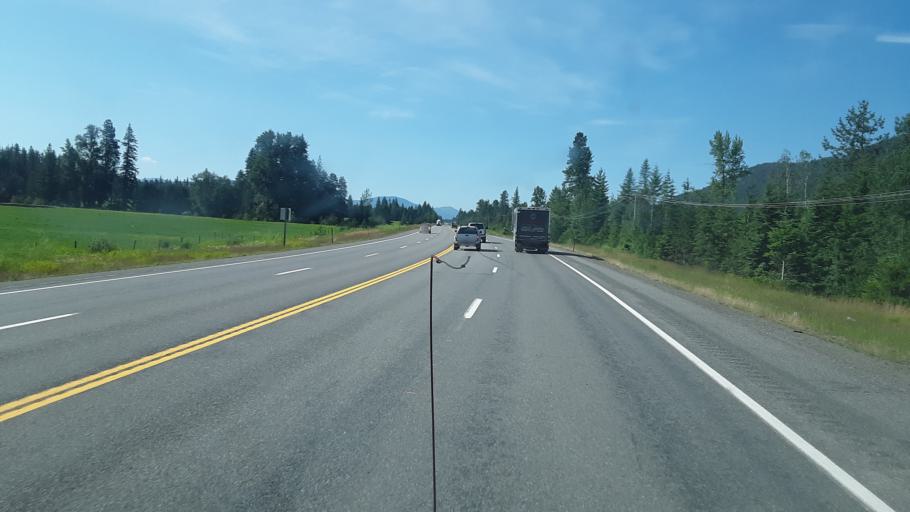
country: US
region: Idaho
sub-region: Bonner County
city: Ponderay
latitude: 48.3743
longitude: -116.5470
